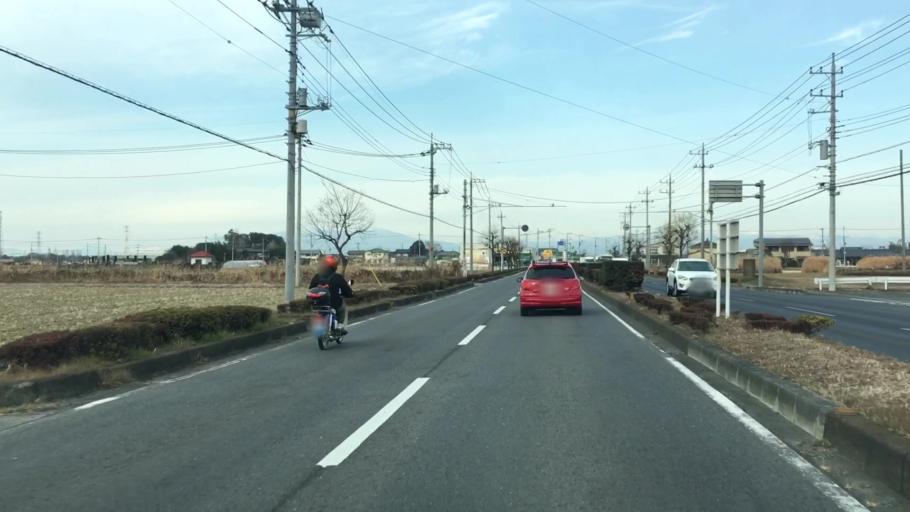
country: JP
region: Saitama
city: Menuma
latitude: 36.2156
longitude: 139.3686
